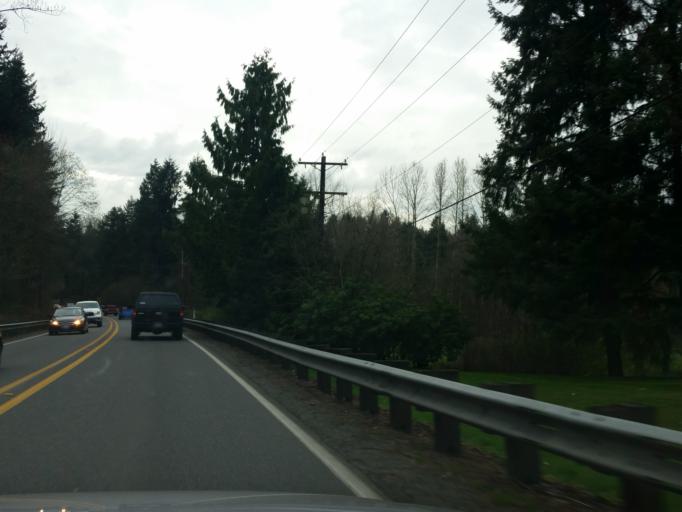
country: US
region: Washington
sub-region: Snohomish County
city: Martha Lake
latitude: 47.8257
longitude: -122.2430
